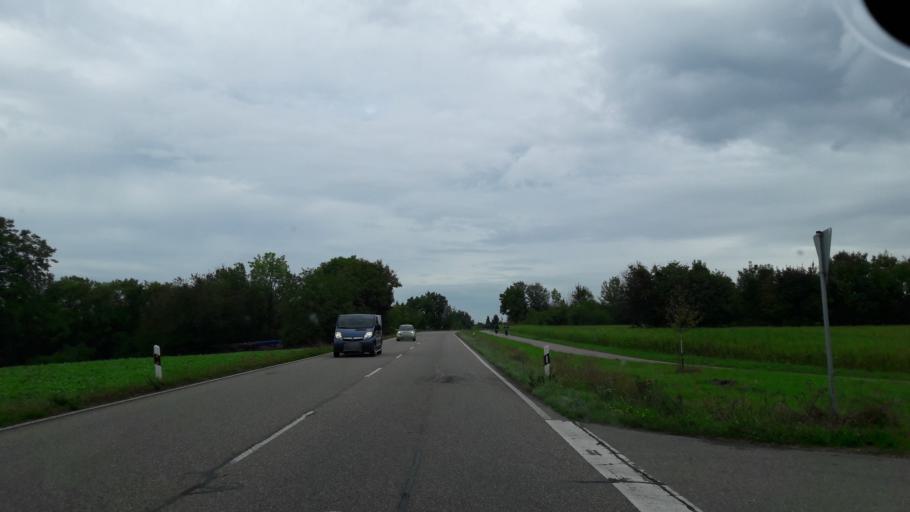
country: DE
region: Baden-Wuerttemberg
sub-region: Karlsruhe Region
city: Kronau
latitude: 49.2319
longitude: 8.6551
